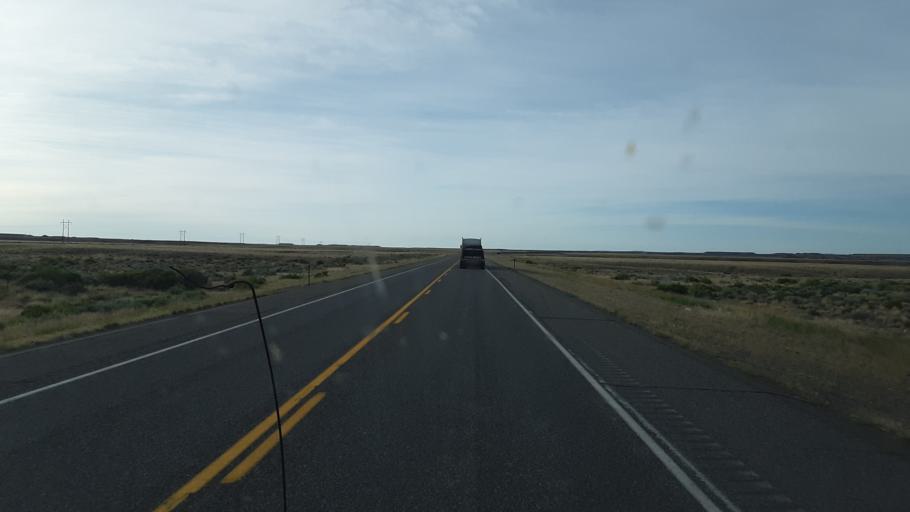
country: US
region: Wyoming
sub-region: Hot Springs County
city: Thermopolis
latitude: 43.3711
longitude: -108.1232
